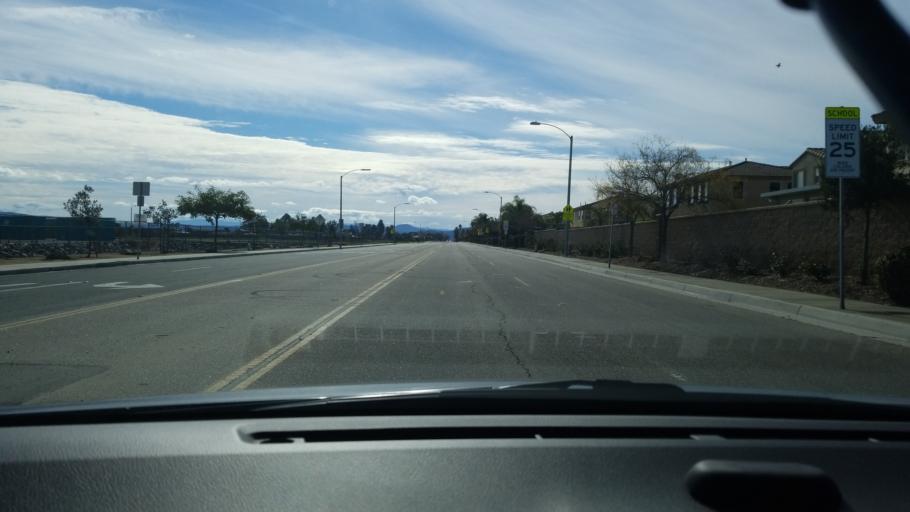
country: US
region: California
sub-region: Riverside County
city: San Jacinto
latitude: 33.7869
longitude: -117.0155
